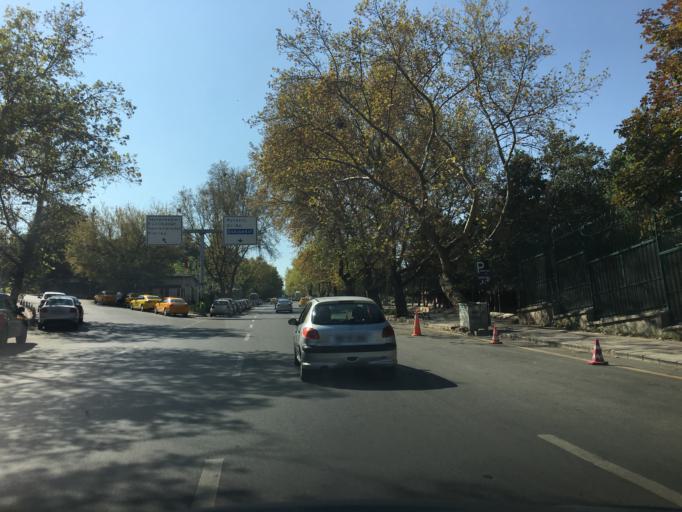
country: TR
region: Ankara
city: Cankaya
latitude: 39.8982
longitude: 32.8632
